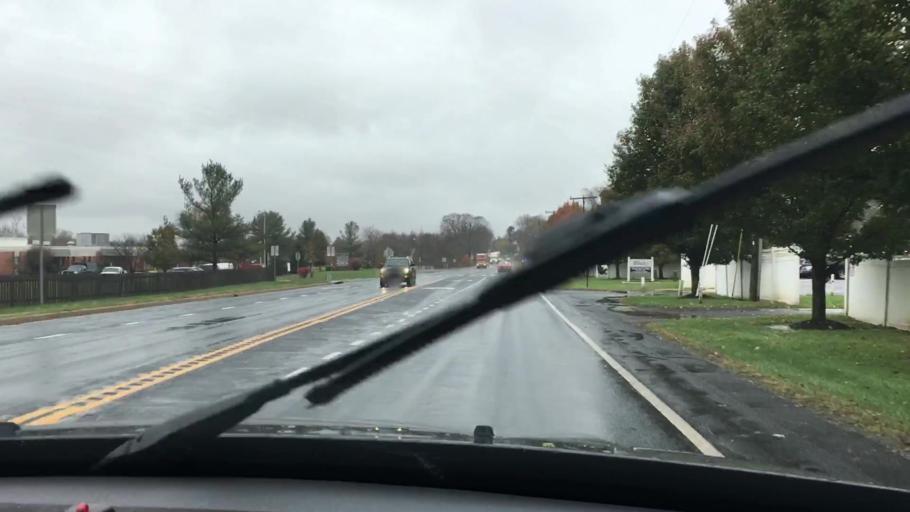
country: US
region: Maryland
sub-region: Frederick County
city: Point of Rocks
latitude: 39.2148
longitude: -77.5349
